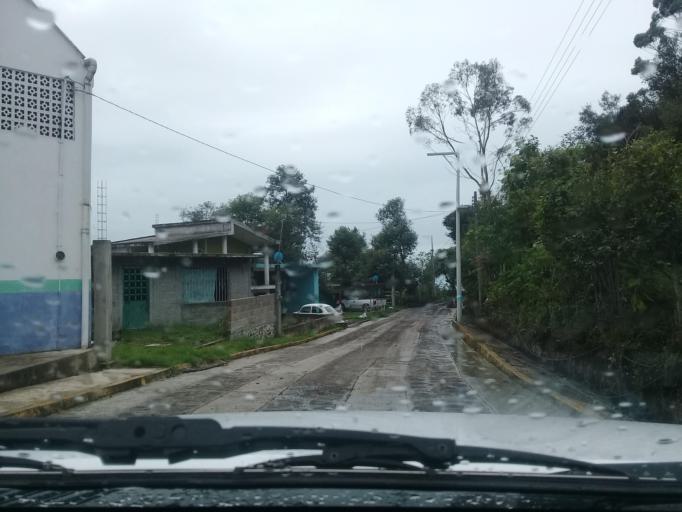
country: MX
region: Veracruz
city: Rafael Lucio
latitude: 19.6137
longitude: -96.9920
